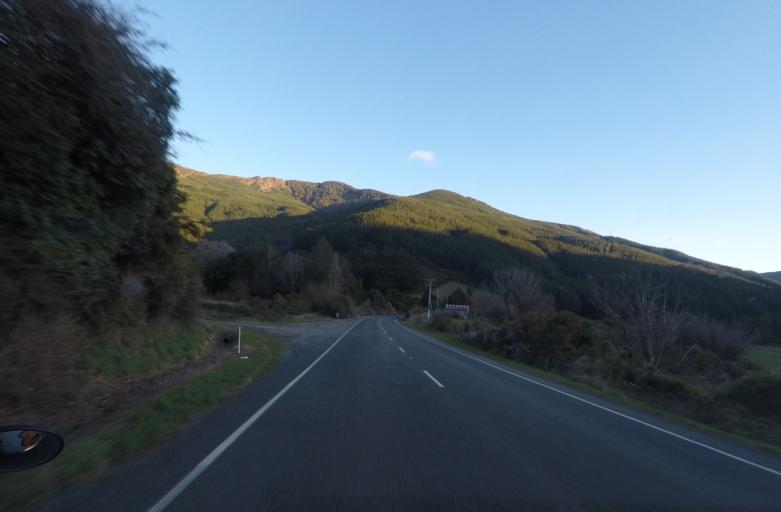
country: NZ
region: Marlborough
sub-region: Marlborough District
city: Picton
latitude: -41.2802
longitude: 173.7276
